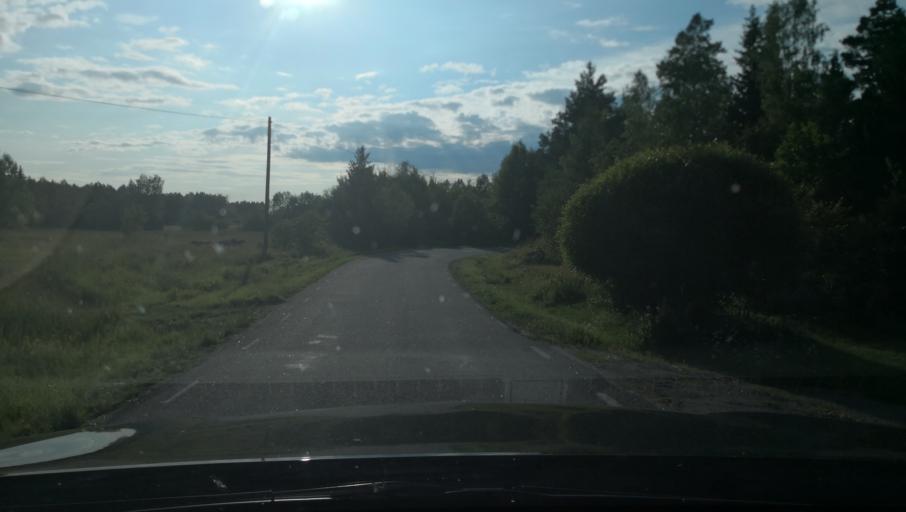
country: SE
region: Uppsala
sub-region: Osthammars Kommun
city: Osterbybruk
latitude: 60.0178
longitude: 17.9246
